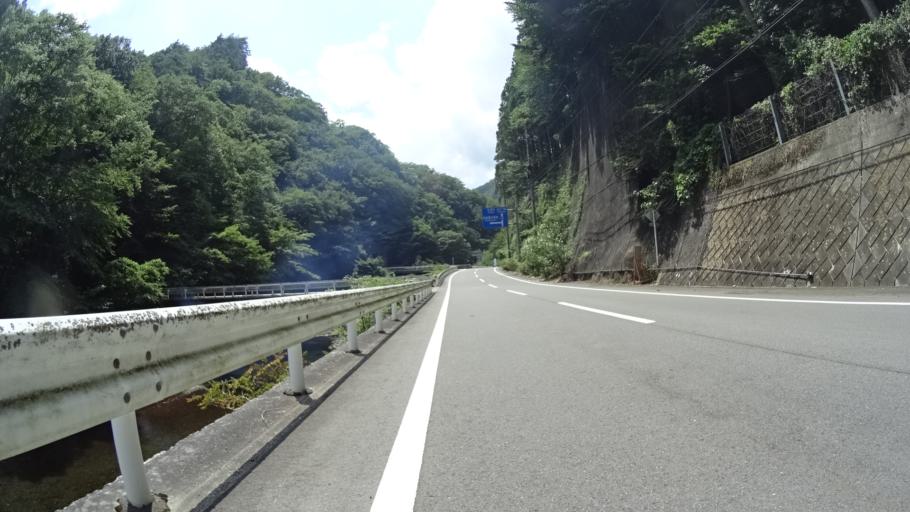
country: JP
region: Gunma
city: Tomioka
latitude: 36.0738
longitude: 138.7066
